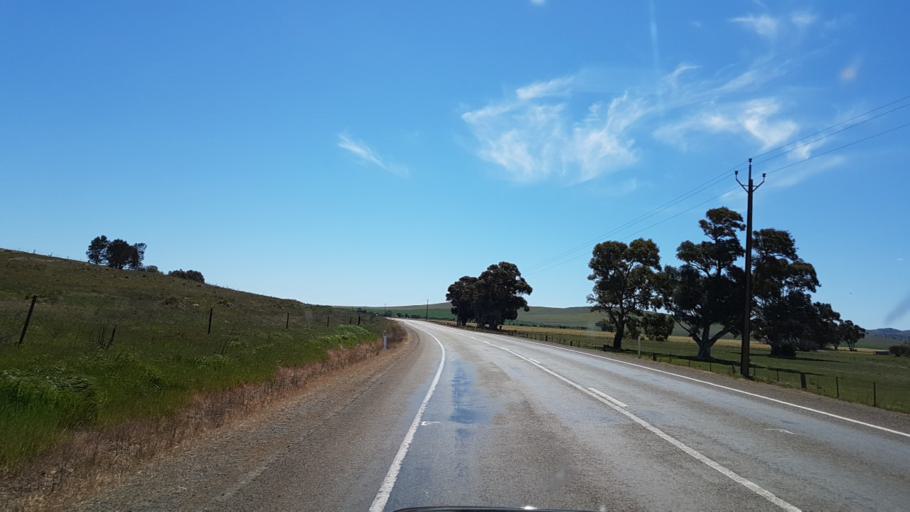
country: AU
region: South Australia
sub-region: Northern Areas
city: Jamestown
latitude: -33.5016
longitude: 138.8992
